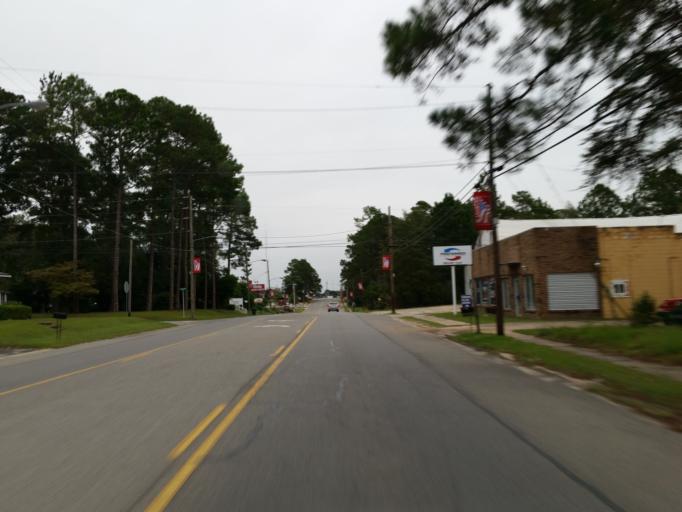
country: US
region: Georgia
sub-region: Turner County
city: Ashburn
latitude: 31.7078
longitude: -83.6483
